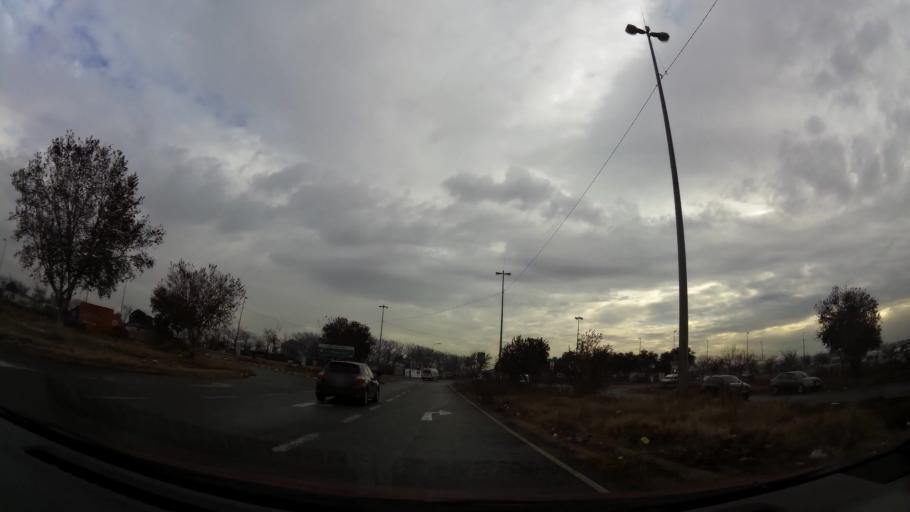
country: ZA
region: Gauteng
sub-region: City of Johannesburg Metropolitan Municipality
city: Soweto
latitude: -26.2911
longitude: 27.8445
